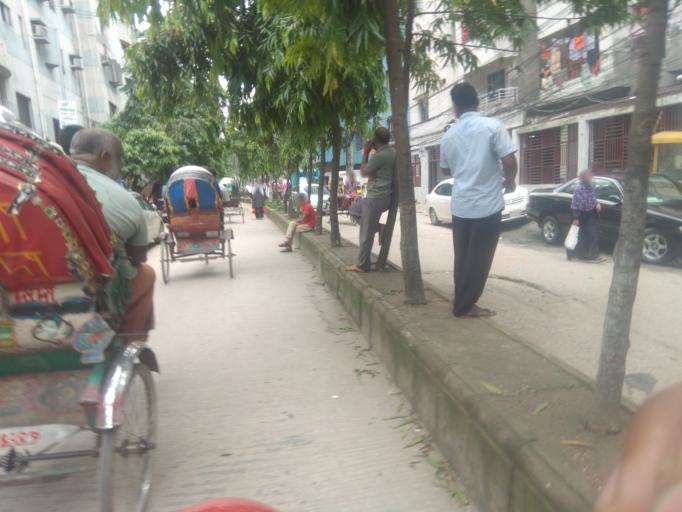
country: BD
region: Dhaka
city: Azimpur
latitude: 23.7428
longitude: 90.3928
